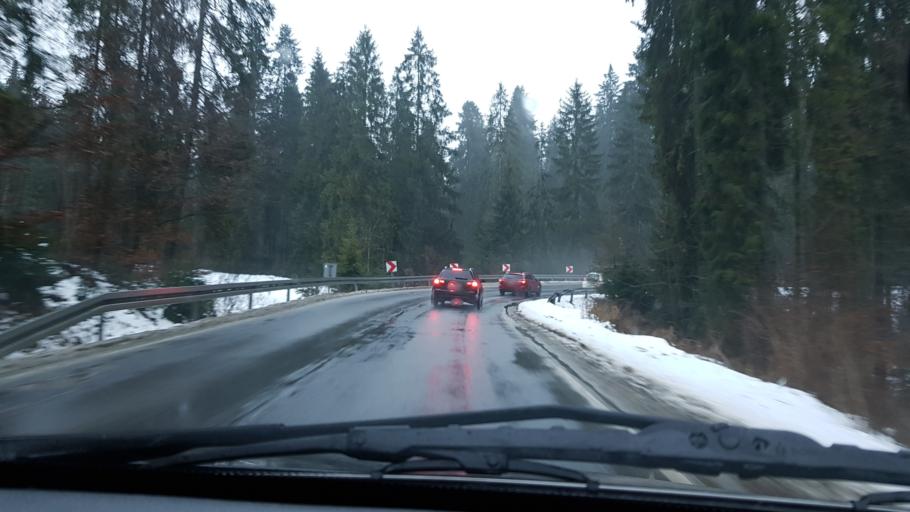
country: PL
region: Lesser Poland Voivodeship
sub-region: Powiat nowotarski
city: Sieniawa
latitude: 49.5146
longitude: 19.8972
